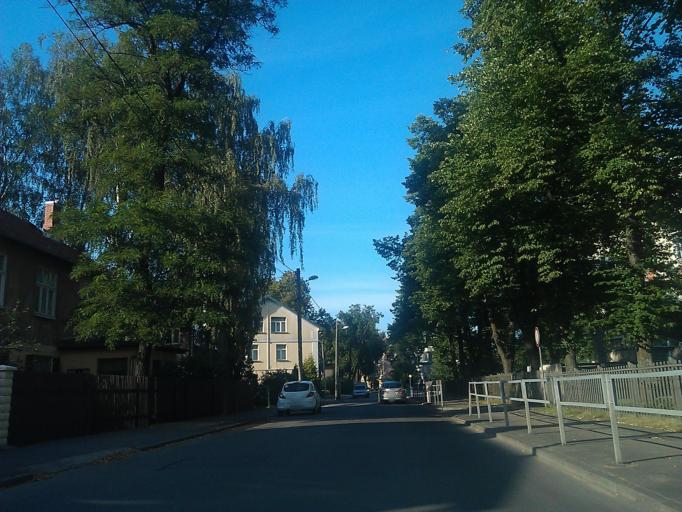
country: LV
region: Riga
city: Jaunciems
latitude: 56.9762
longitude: 24.1838
